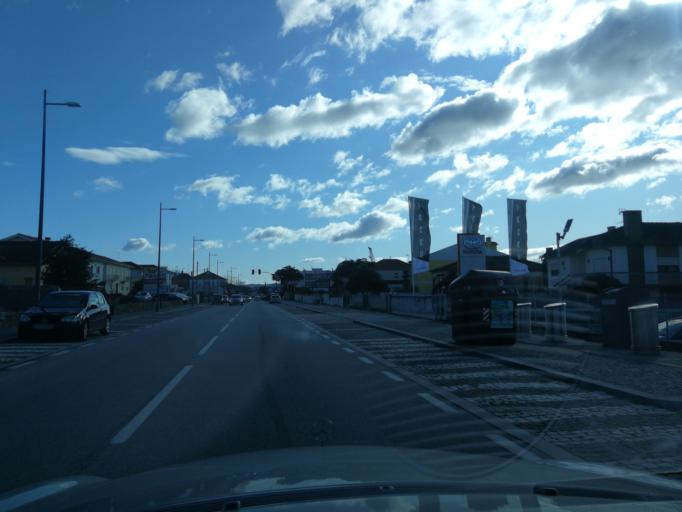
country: PT
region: Viana do Castelo
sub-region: Viana do Castelo
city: Viana do Castelo
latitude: 41.6992
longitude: -8.8458
